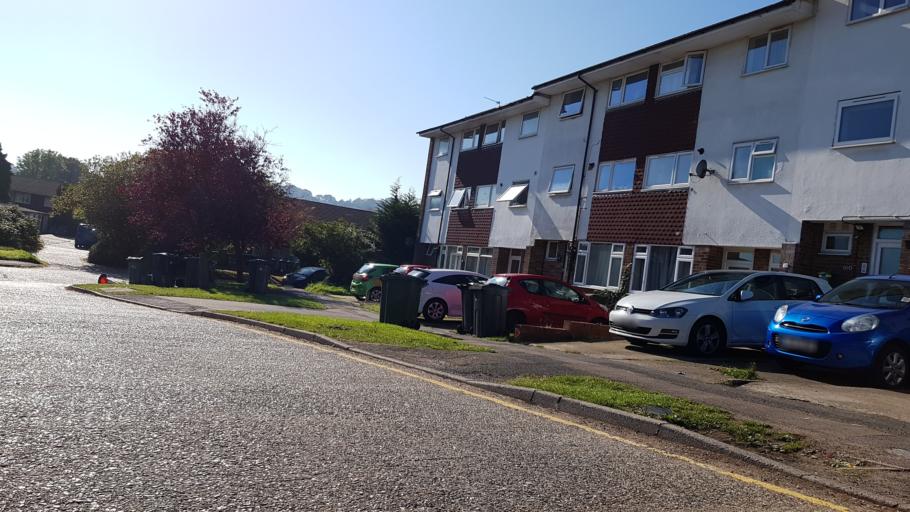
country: GB
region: England
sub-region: Surrey
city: Guildford
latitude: 51.2396
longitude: -0.5850
